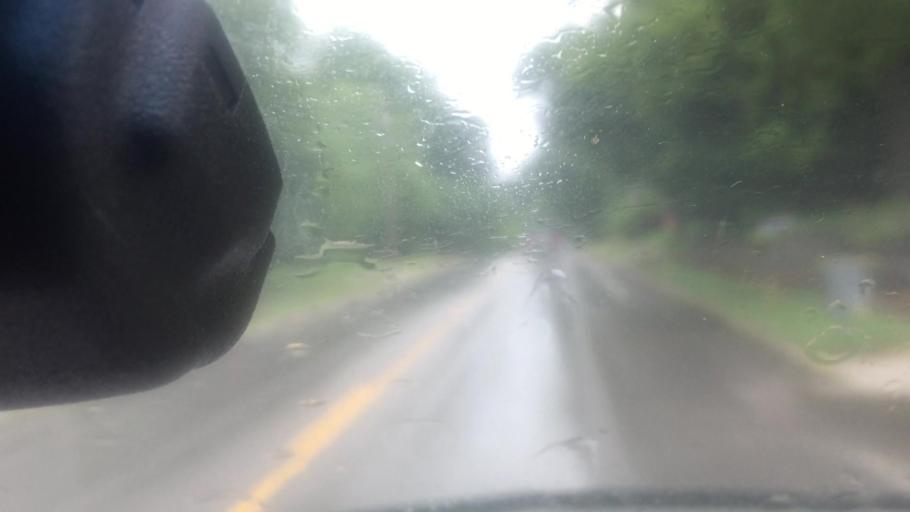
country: US
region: Illinois
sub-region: Madison County
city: Edwardsville
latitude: 38.8130
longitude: -89.9454
